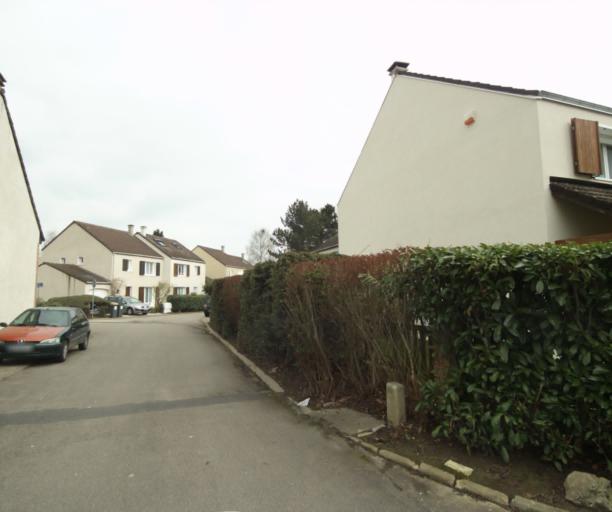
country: FR
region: Ile-de-France
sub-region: Departement du Val-d'Oise
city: Osny
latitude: 49.0497
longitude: 2.0478
